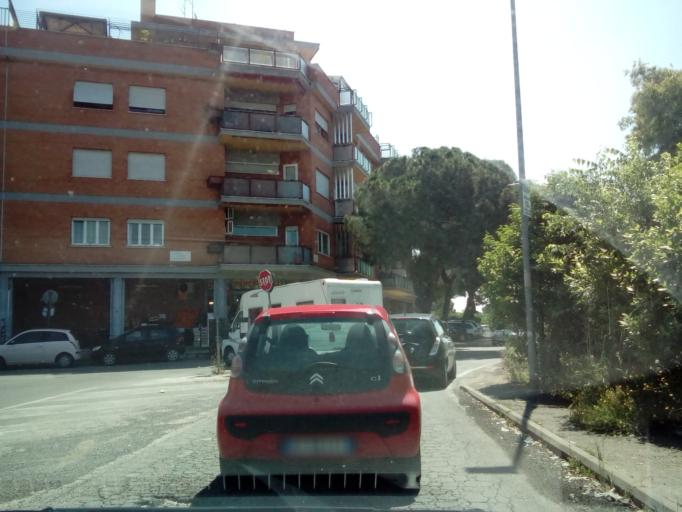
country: IT
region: Latium
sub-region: Citta metropolitana di Roma Capitale
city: Rome
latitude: 41.8915
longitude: 12.5846
